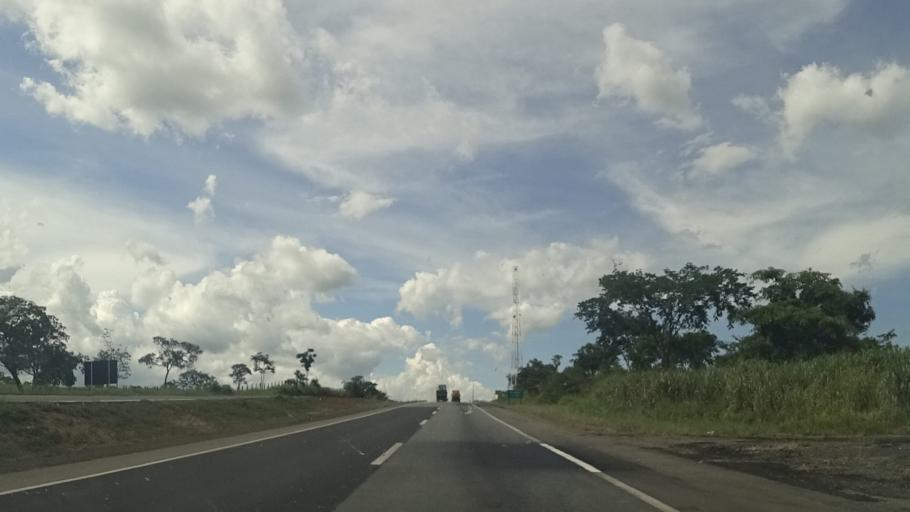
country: BR
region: Goias
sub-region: Piracanjuba
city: Piracanjuba
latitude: -17.2947
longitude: -49.2344
